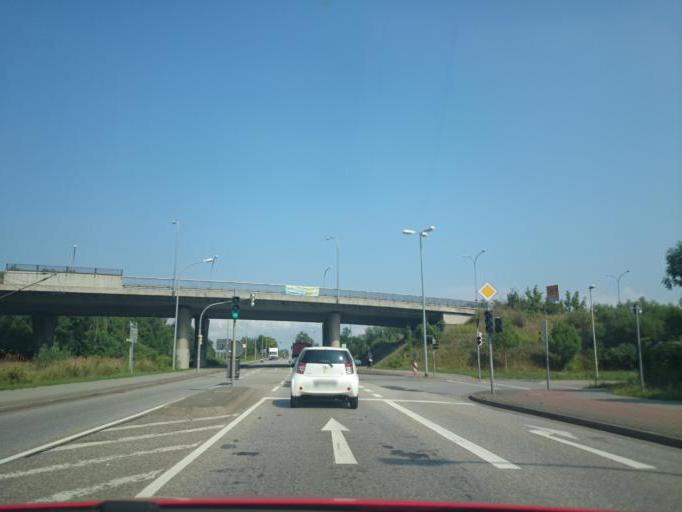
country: DE
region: Mecklenburg-Vorpommern
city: Stralsund
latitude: 54.3045
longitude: 13.0484
